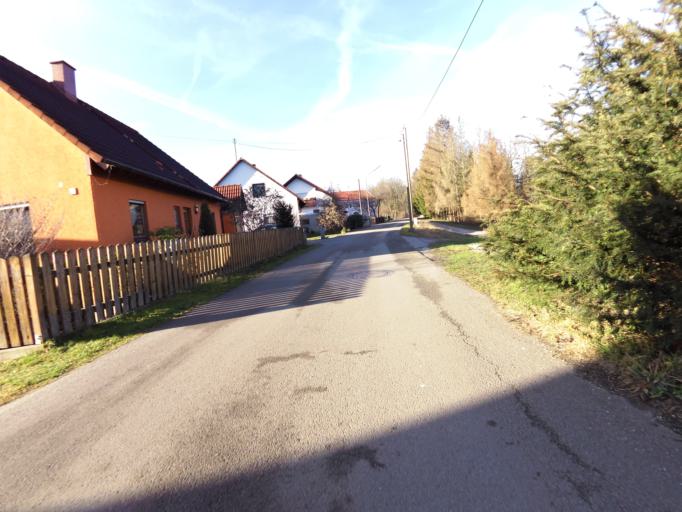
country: DE
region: Bavaria
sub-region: Upper Bavaria
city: Wang
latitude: 48.4958
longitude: 11.9660
